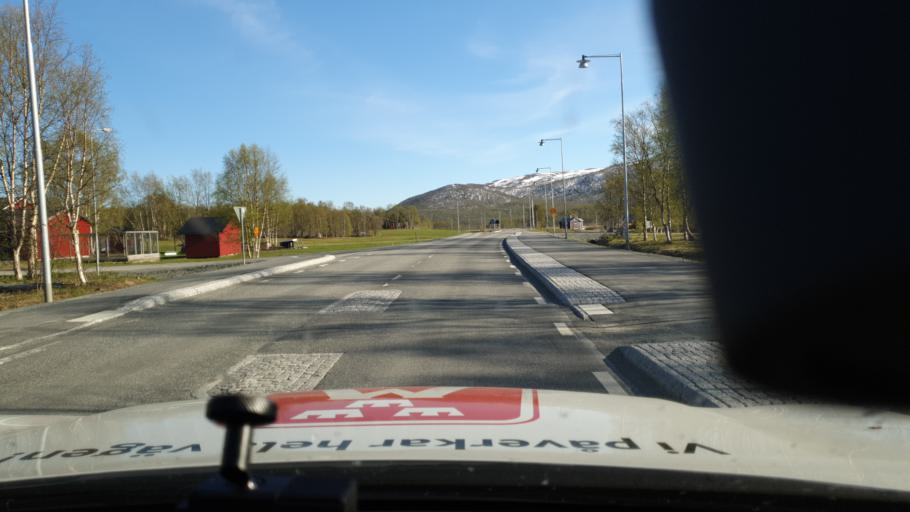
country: NO
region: Nordland
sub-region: Rana
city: Mo i Rana
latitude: 65.8108
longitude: 15.0885
